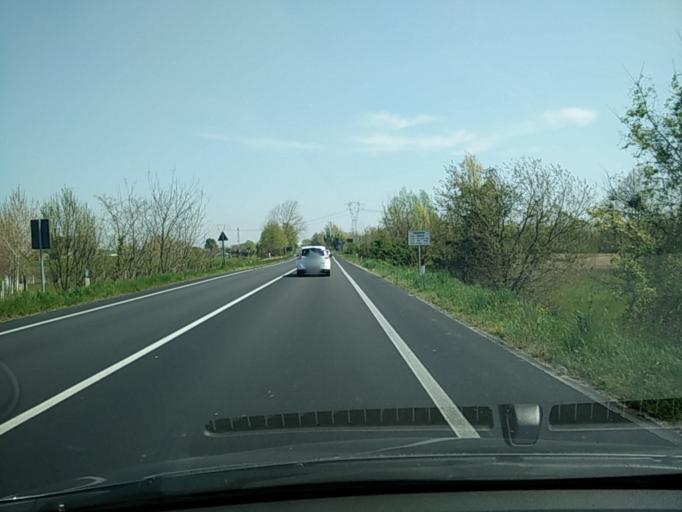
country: IT
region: Veneto
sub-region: Provincia di Treviso
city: Biancade
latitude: 45.6391
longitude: 12.3622
